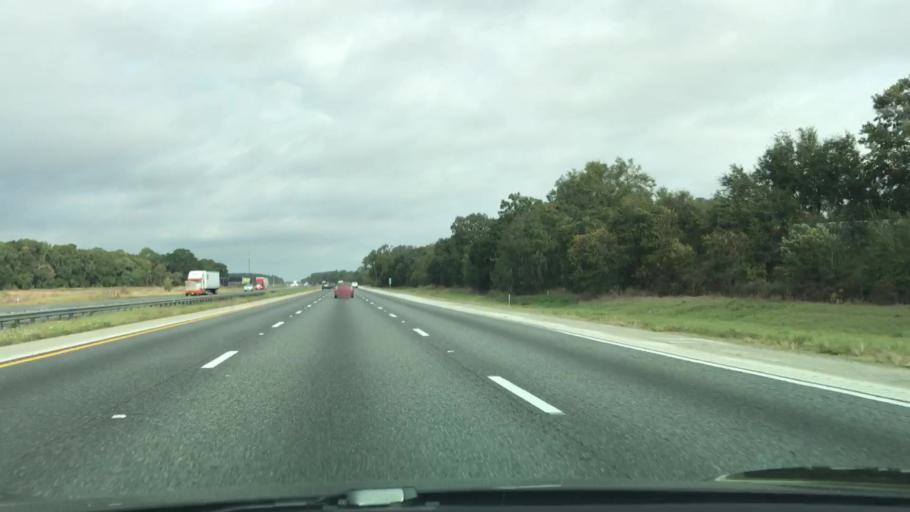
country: US
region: Florida
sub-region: Marion County
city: Belleview
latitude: 28.9613
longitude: -82.1274
